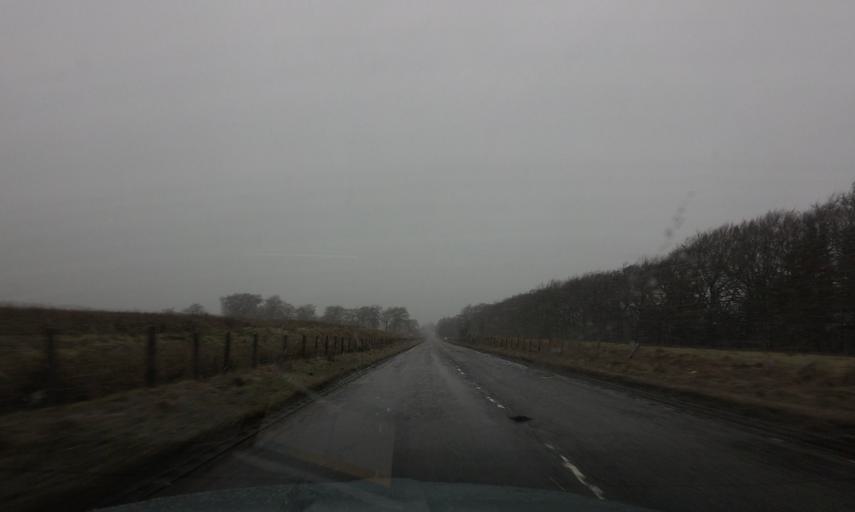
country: GB
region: Scotland
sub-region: North Lanarkshire
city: Shotts
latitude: 55.8473
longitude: -3.8317
